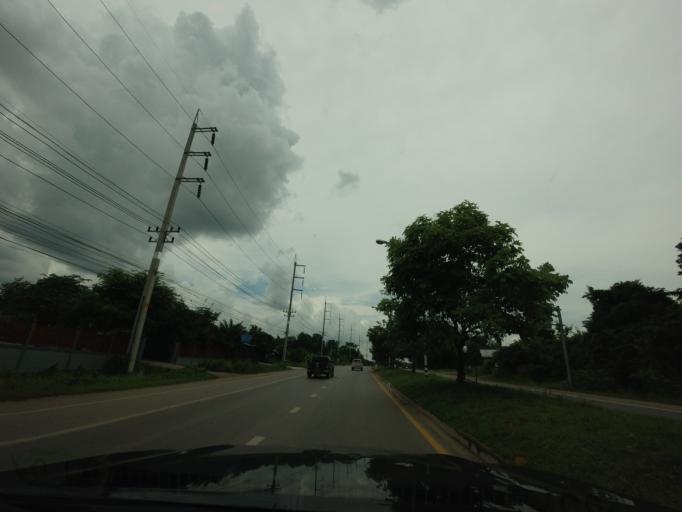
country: TH
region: Changwat Nong Bua Lamphu
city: Nong Bua Lamphu
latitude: 17.2138
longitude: 102.4102
